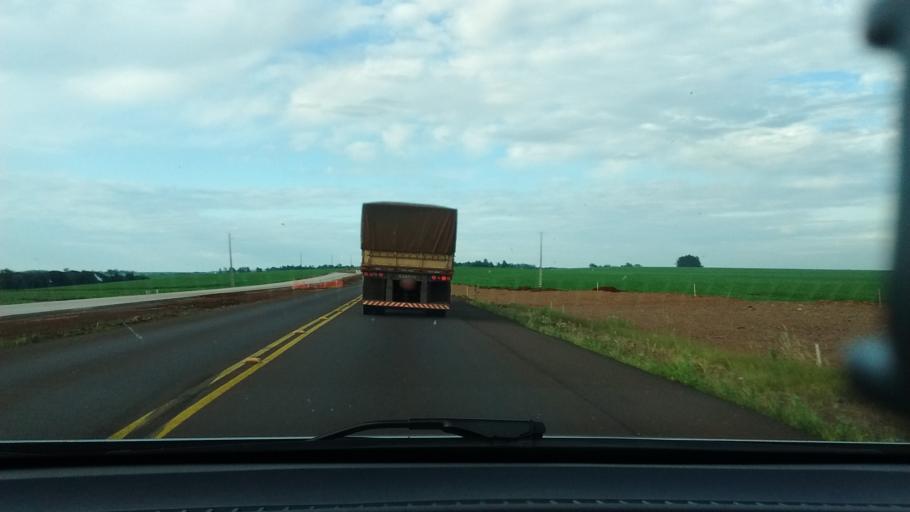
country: BR
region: Parana
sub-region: Cascavel
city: Cascavel
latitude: -25.0712
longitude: -53.5727
